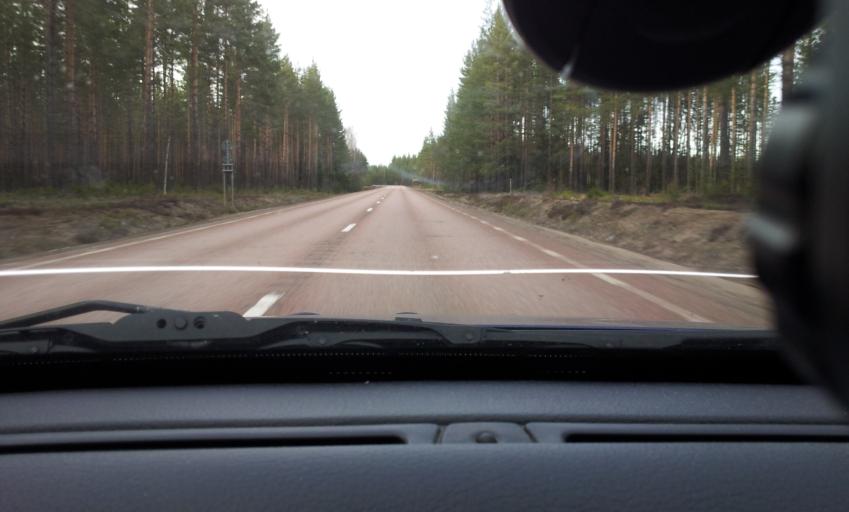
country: SE
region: Gaevleborg
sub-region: Ljusdals Kommun
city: Farila
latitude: 61.8442
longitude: 15.7508
